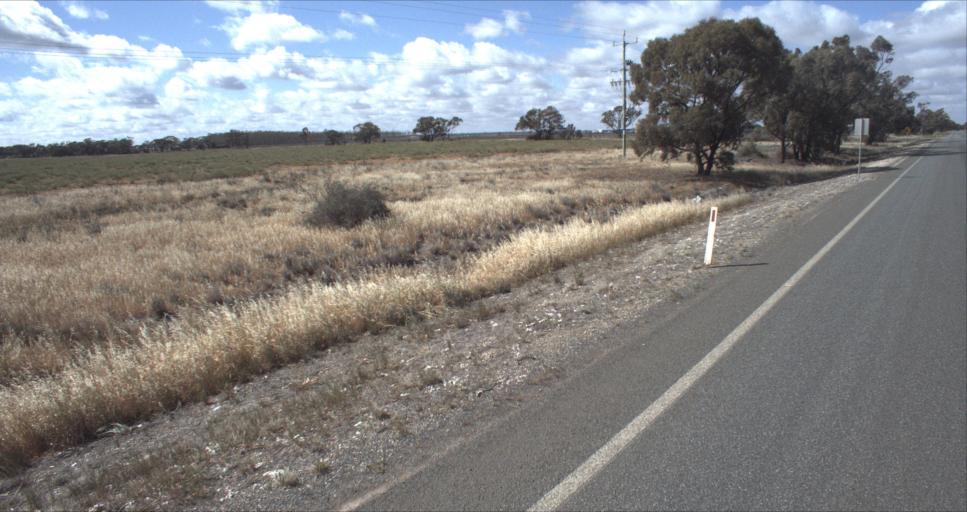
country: AU
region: New South Wales
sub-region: Murrumbidgee Shire
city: Darlington Point
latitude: -34.5555
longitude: 146.1699
